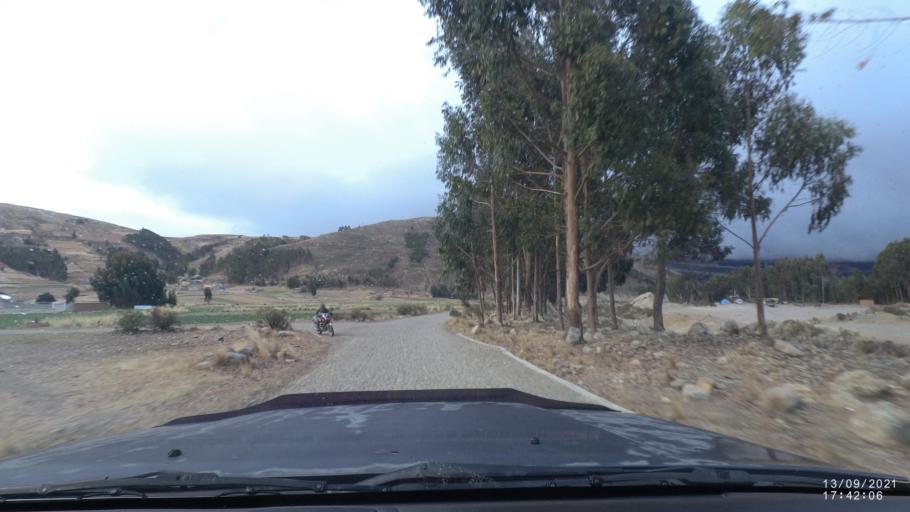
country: BO
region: Cochabamba
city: Colomi
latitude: -17.3679
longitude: -65.8147
